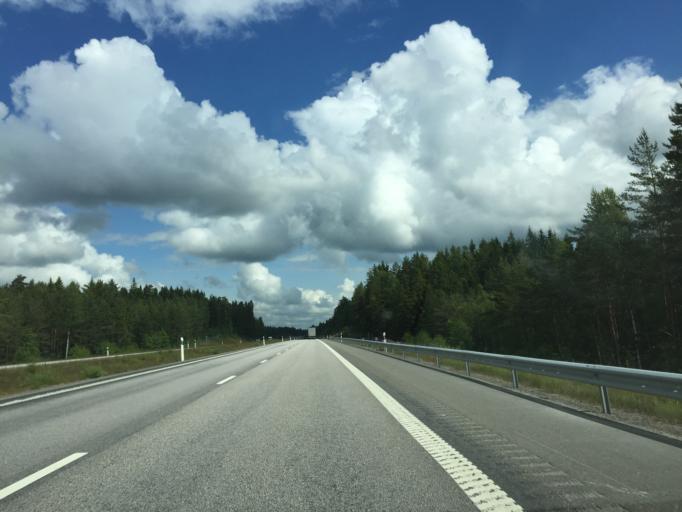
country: SE
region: OErebro
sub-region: Lindesbergs Kommun
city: Fellingsbro
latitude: 59.3539
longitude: 15.5620
